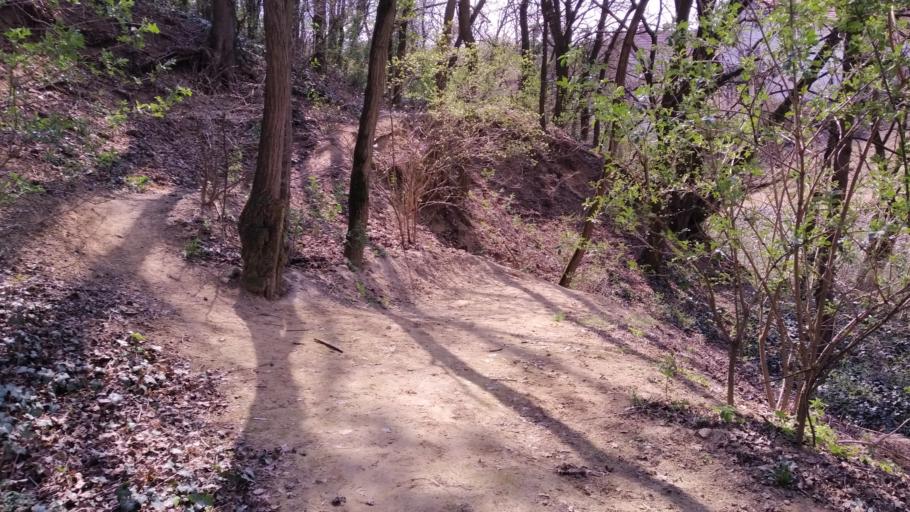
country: HU
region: Pest
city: Budakalasz
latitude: 47.6148
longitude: 19.0437
